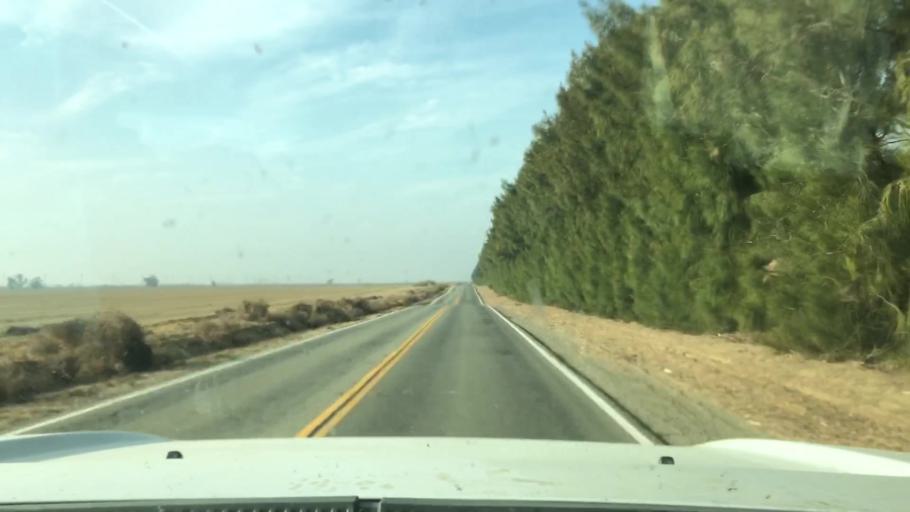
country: US
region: California
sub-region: Kern County
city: Lost Hills
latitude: 35.5030
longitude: -119.7424
